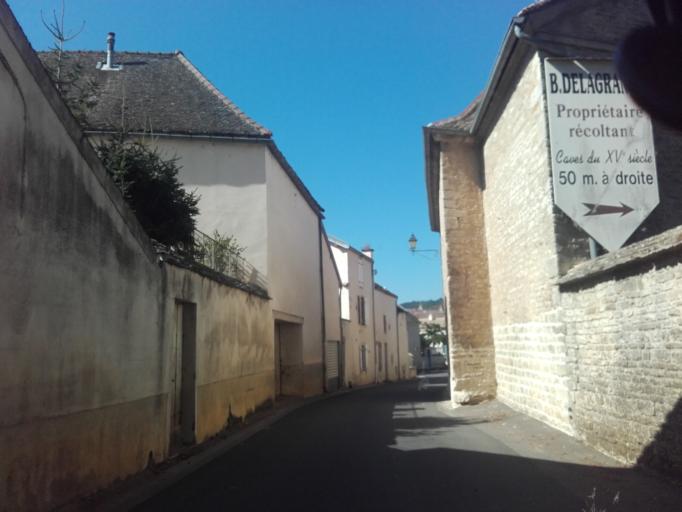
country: FR
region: Bourgogne
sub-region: Departement de la Cote-d'Or
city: Meursault
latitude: 46.9808
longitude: 4.7690
